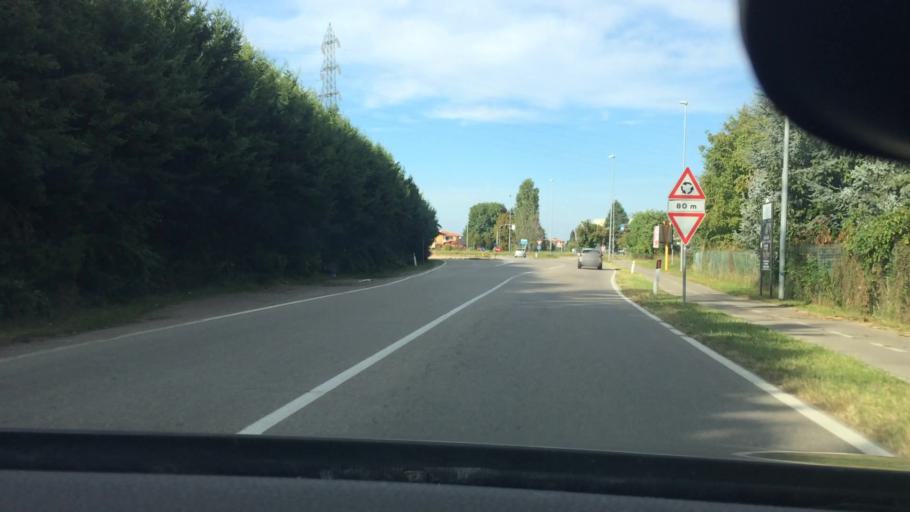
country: IT
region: Lombardy
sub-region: Citta metropolitana di Milano
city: Villa Cortese
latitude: 45.5571
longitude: 8.8878
